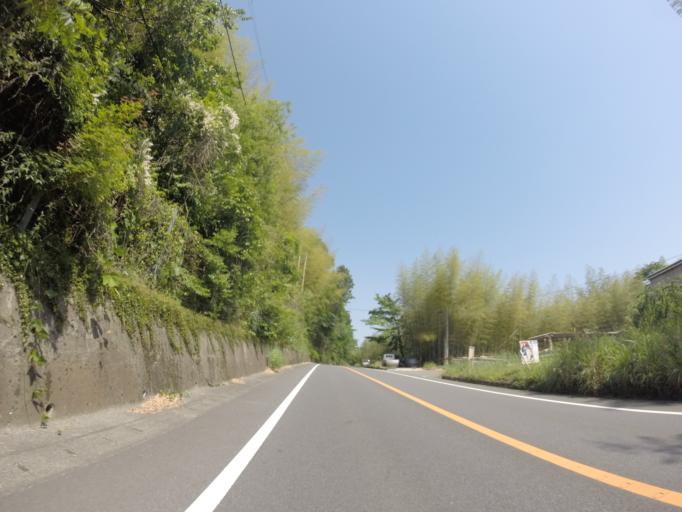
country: JP
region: Shizuoka
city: Fujinomiya
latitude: 35.1992
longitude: 138.5781
